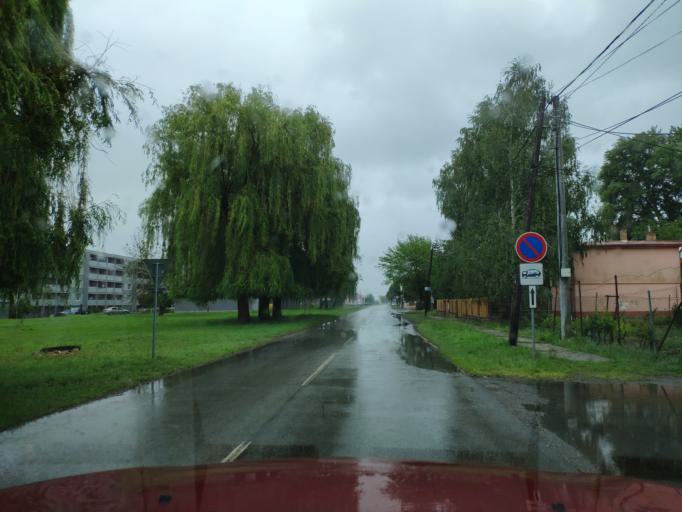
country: SK
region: Kosicky
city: Cierna nad Tisou
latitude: 48.4197
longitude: 22.0929
